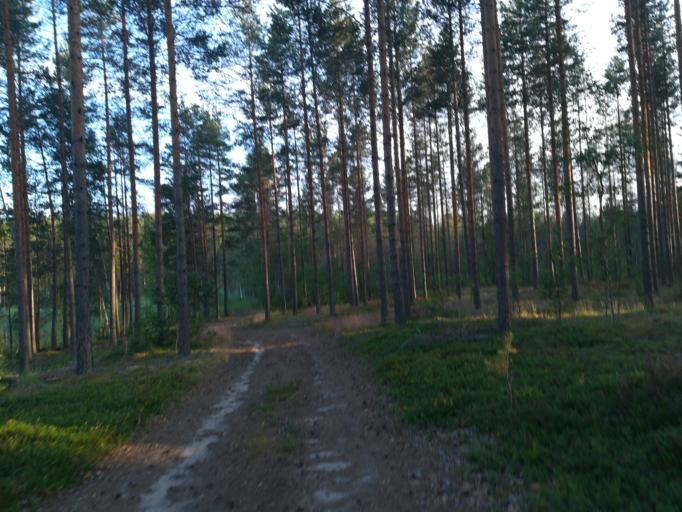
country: FI
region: Southern Savonia
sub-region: Mikkeli
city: Puumala
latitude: 61.4322
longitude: 28.4639
